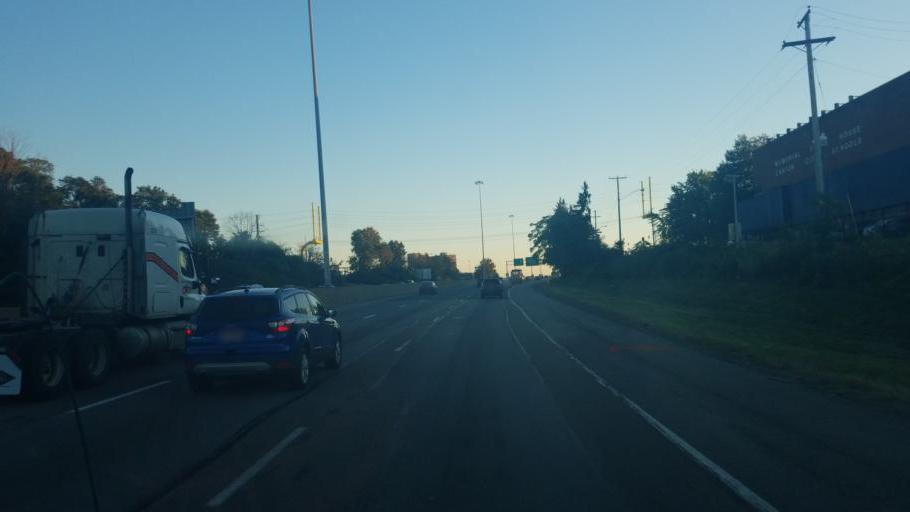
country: US
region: Ohio
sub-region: Stark County
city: Canton
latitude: 40.8193
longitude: -81.3964
